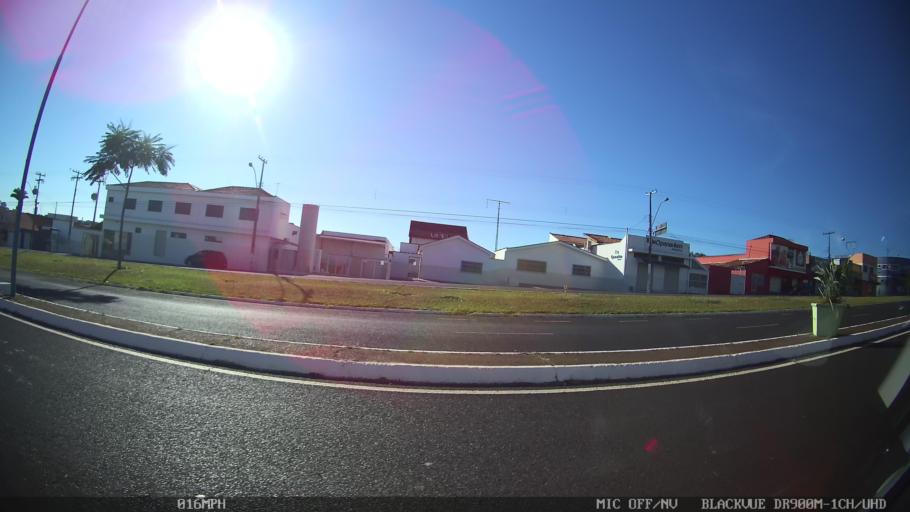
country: BR
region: Sao Paulo
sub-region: Franca
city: Franca
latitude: -20.5586
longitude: -47.3957
